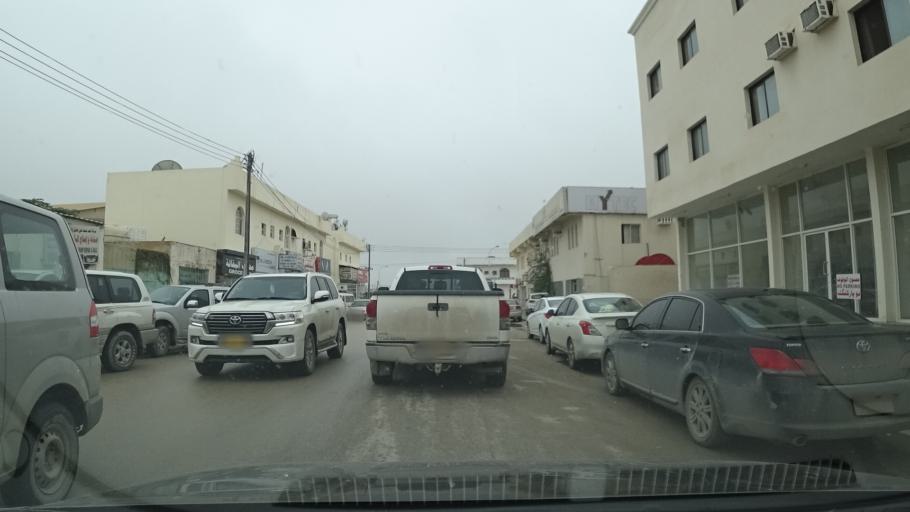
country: OM
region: Zufar
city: Salalah
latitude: 17.0224
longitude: 54.0507
